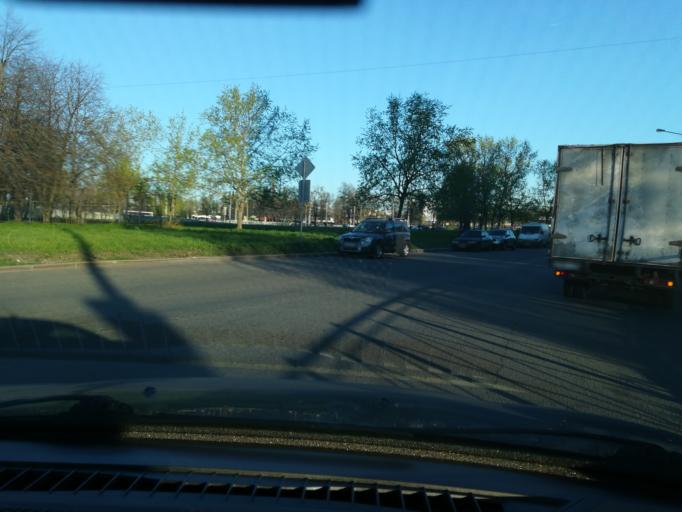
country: RU
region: St.-Petersburg
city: Avtovo
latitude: 59.8625
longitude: 30.2549
